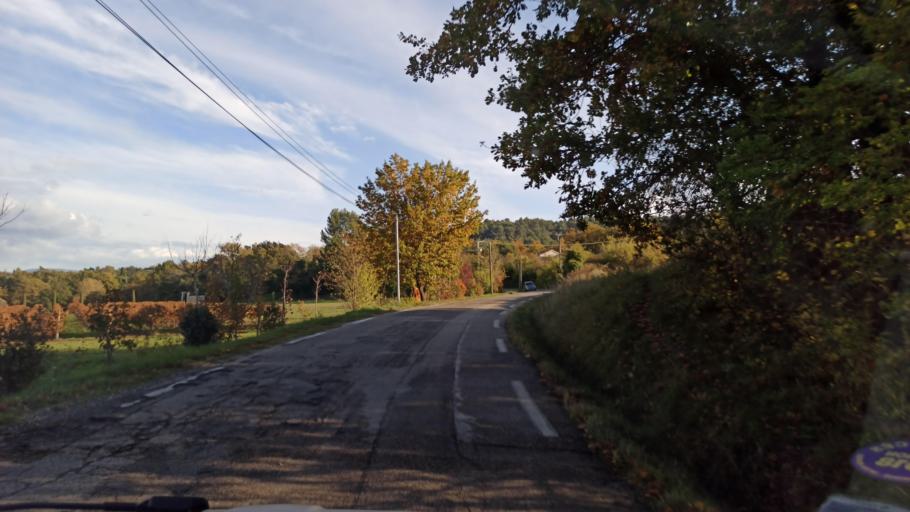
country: FR
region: Provence-Alpes-Cote d'Azur
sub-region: Departement du Vaucluse
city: Goult
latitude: 43.8383
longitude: 5.2619
